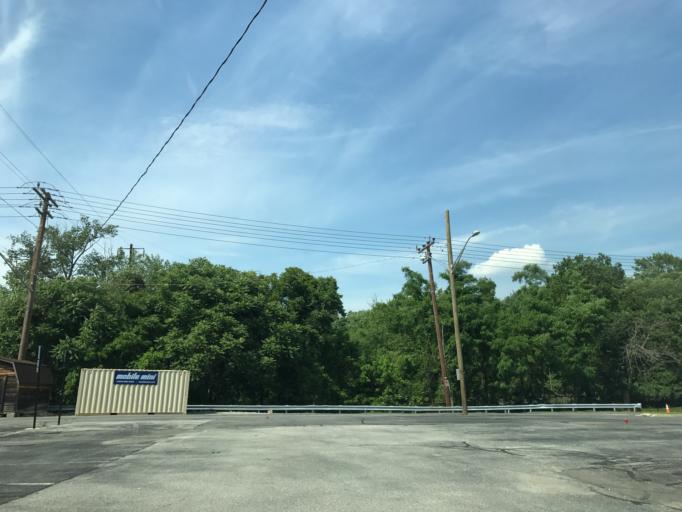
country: US
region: Maryland
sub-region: Anne Arundel County
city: Odenton
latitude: 39.0870
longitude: -76.7059
